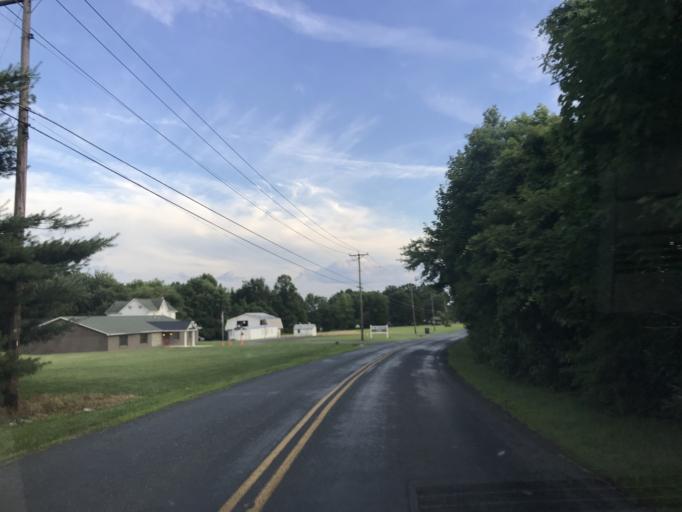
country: US
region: Maryland
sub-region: Harford County
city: Perryman
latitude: 39.5118
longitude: -76.2065
